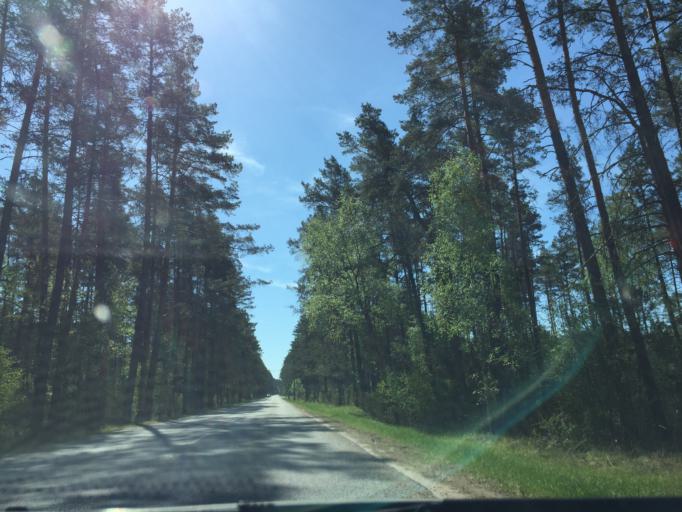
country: LV
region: Garkalne
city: Garkalne
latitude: 57.0318
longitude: 24.4237
